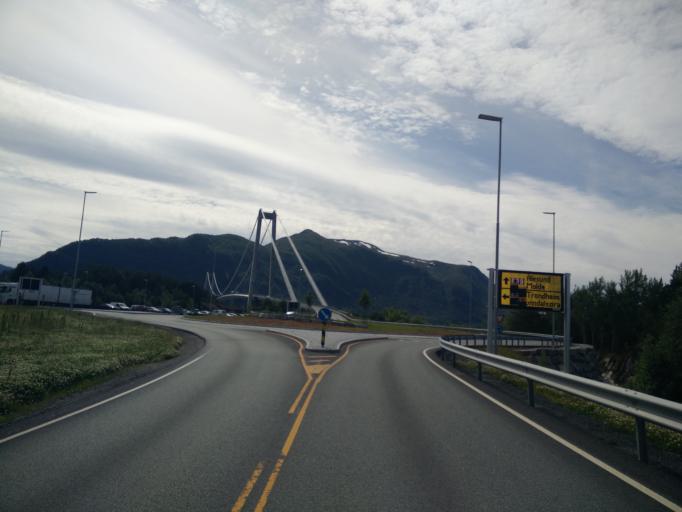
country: NO
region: More og Romsdal
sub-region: Kristiansund
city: Rensvik
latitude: 62.9763
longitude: 7.7888
